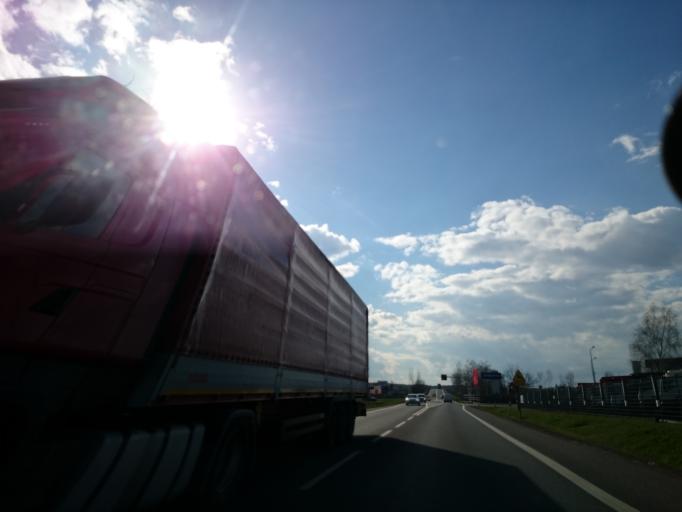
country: PL
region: Opole Voivodeship
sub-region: Powiat opolski
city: Dabrowa
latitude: 50.6895
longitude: 17.7658
